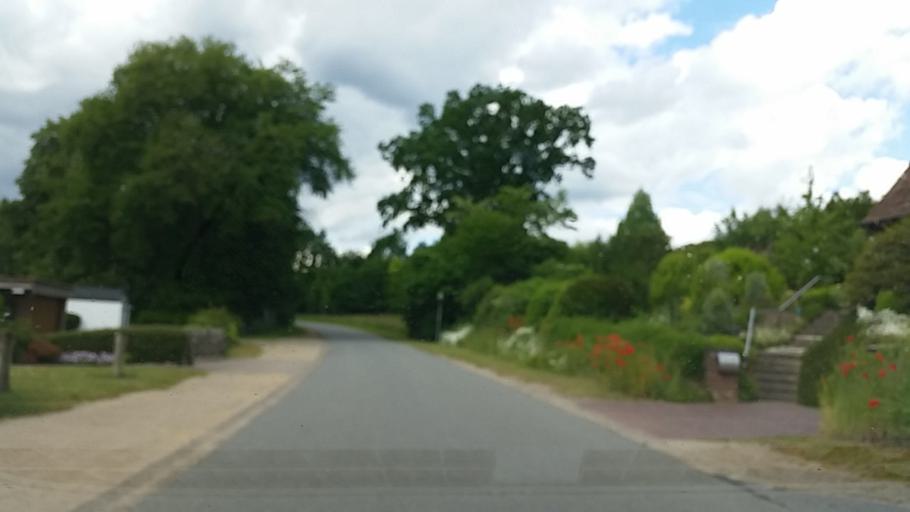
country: DE
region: Schleswig-Holstein
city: Dahmker
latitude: 53.6052
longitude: 10.4475
